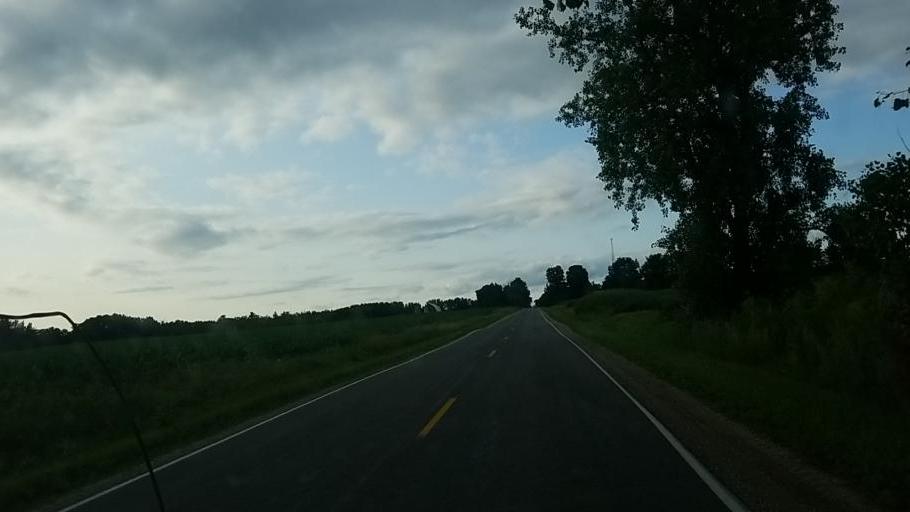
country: US
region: Michigan
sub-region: Montcalm County
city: Lakeview
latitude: 43.3449
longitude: -85.3234
